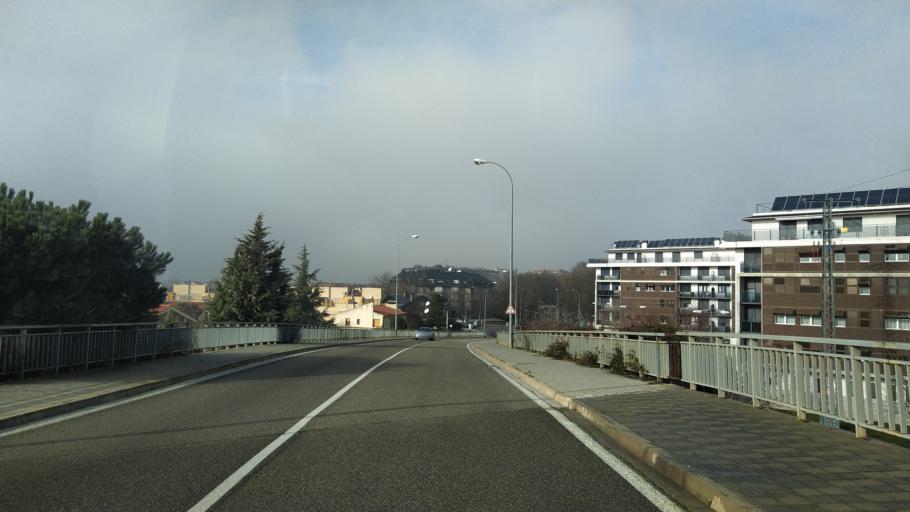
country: ES
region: Castille and Leon
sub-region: Provincia de Palencia
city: Palencia
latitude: 41.9937
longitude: -4.5145
